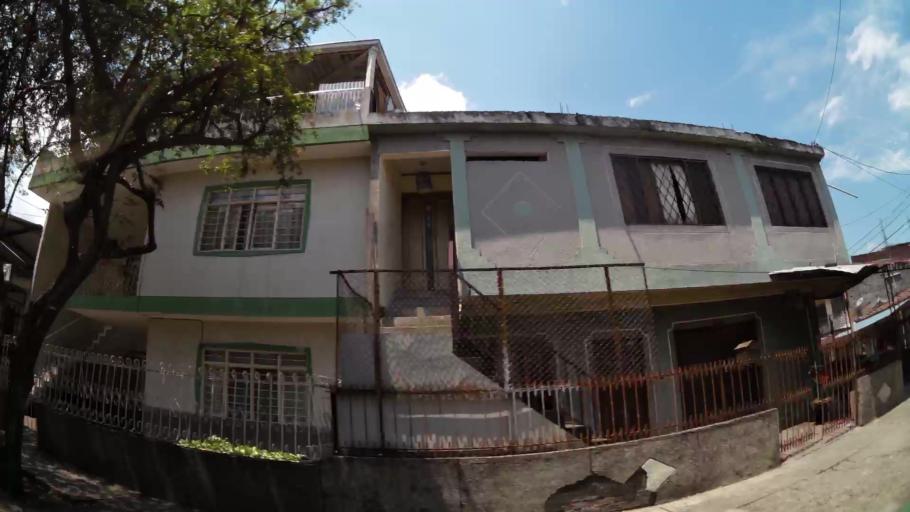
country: CO
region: Valle del Cauca
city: Cali
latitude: 3.4484
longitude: -76.5085
